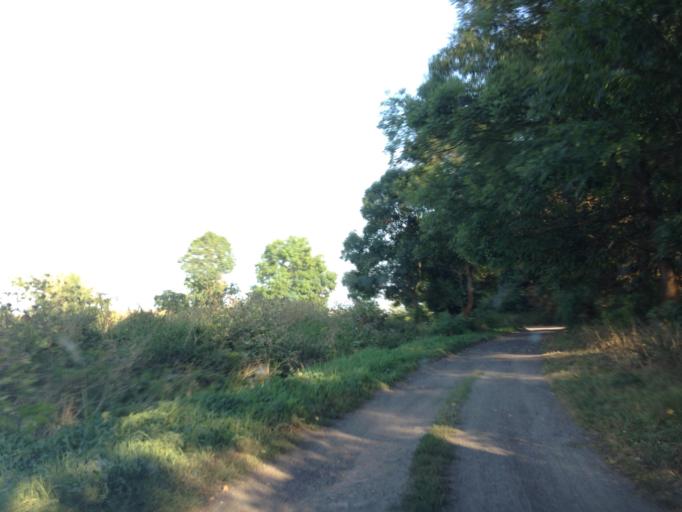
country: PL
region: Kujawsko-Pomorskie
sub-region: Powiat brodnicki
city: Brodnica
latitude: 53.2865
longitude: 19.4195
